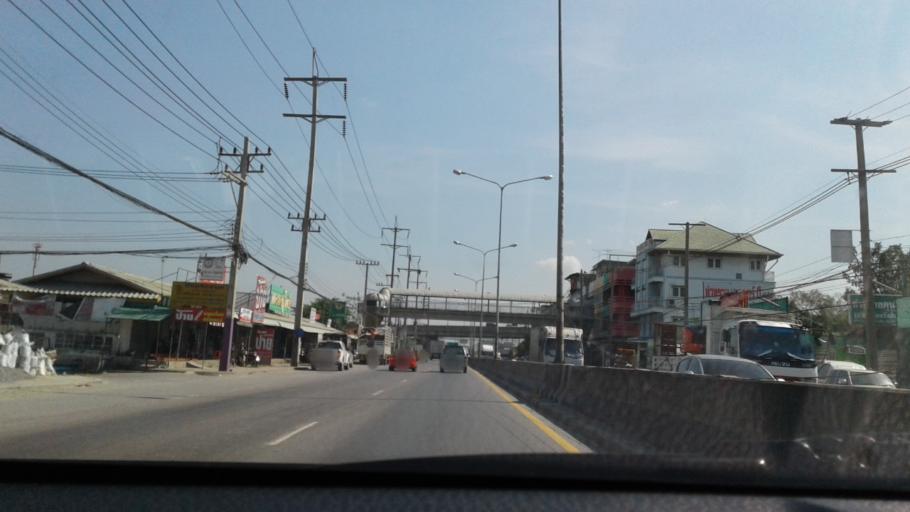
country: TH
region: Phra Nakhon Si Ayutthaya
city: Ban Bang Kadi Pathum Thani
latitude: 13.9675
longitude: 100.5484
